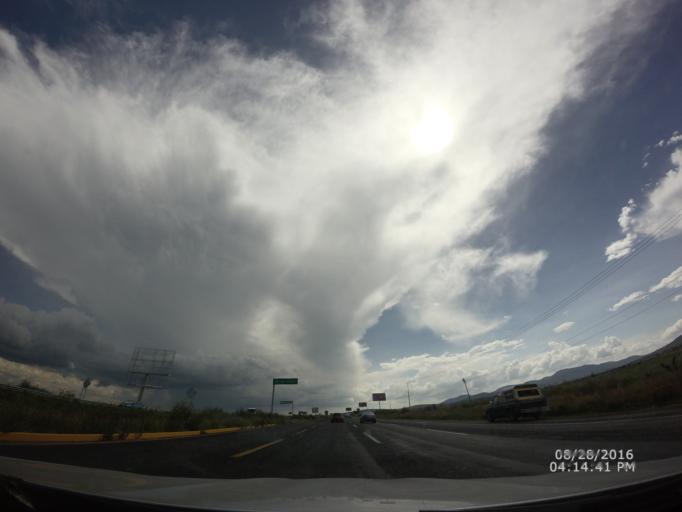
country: MX
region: Hidalgo
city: Acayuca
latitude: 20.0057
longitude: -98.8257
